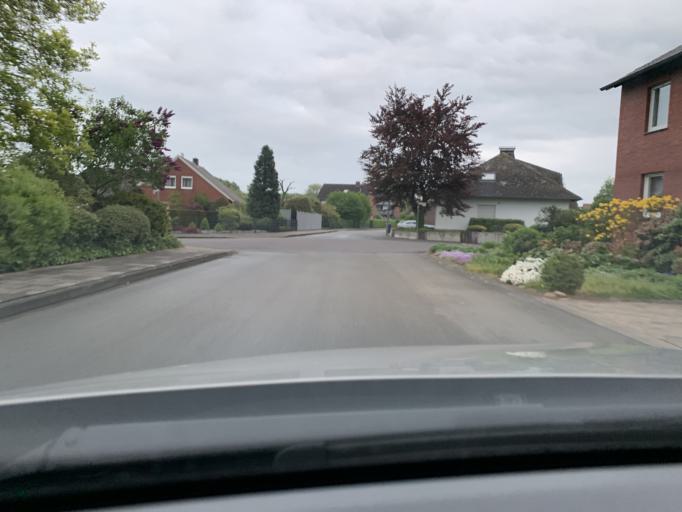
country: DE
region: North Rhine-Westphalia
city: Rietberg
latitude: 51.8013
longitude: 8.3796
